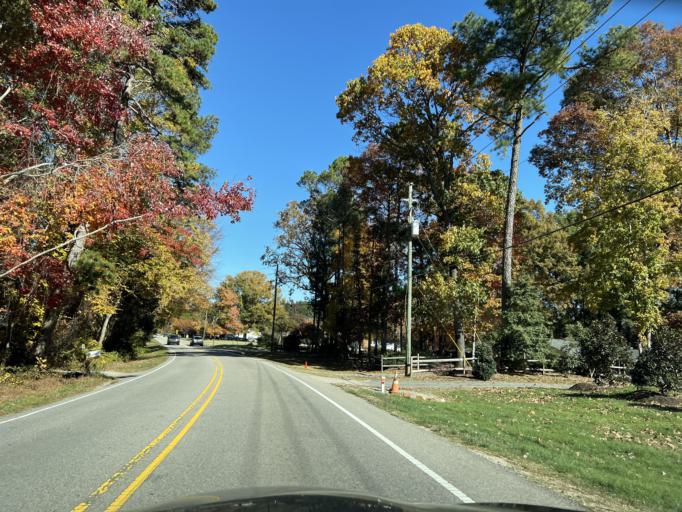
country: US
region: North Carolina
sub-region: Wake County
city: Garner
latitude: 35.6832
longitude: -78.6968
